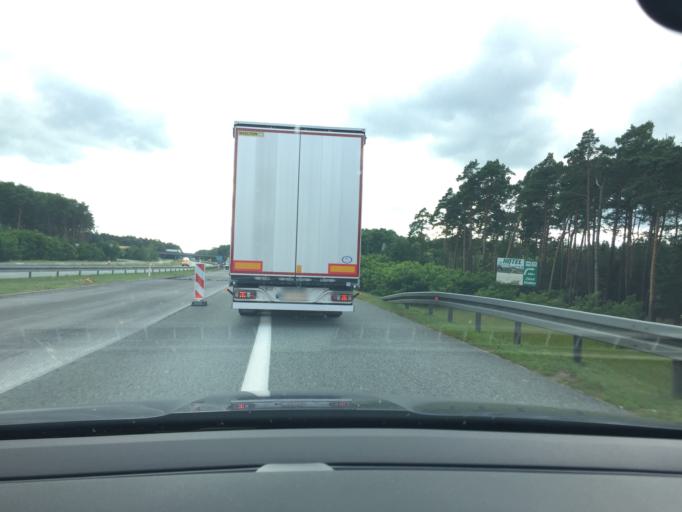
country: PL
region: Lubusz
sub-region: Powiat slubicki
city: Slubice
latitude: 52.3259
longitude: 14.6259
